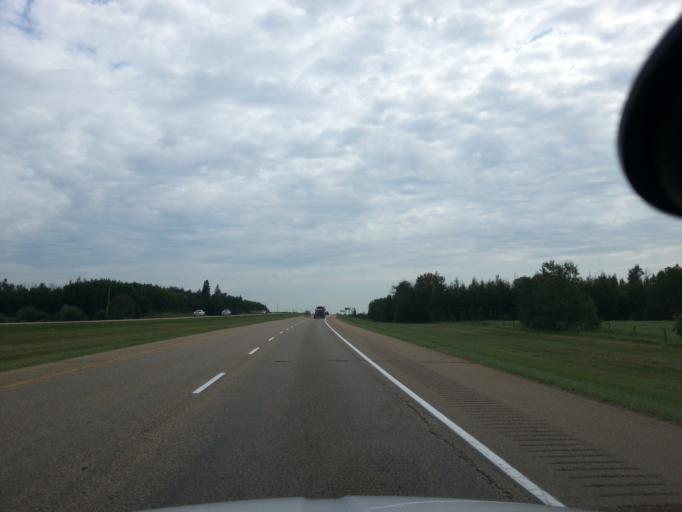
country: CA
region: Alberta
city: Fort Saskatchewan
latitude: 53.5698
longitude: -113.0900
